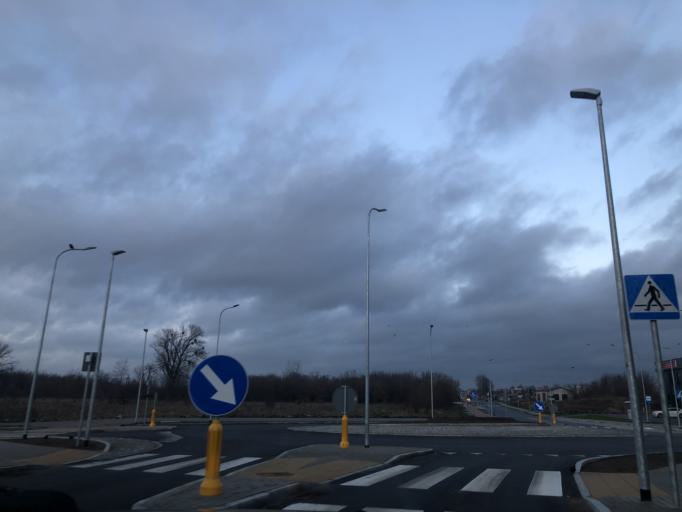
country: PL
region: Podlasie
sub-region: Lomza
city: Lomza
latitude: 53.1692
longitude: 22.0592
